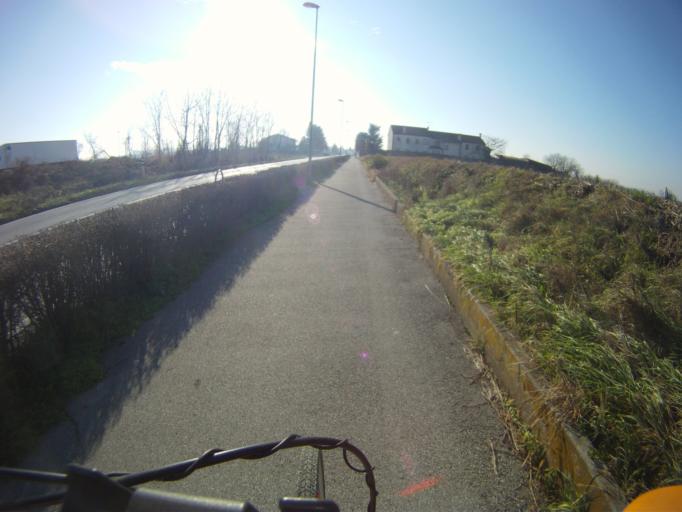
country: IT
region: Veneto
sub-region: Provincia di Padova
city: Brugine
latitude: 45.3051
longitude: 11.9967
